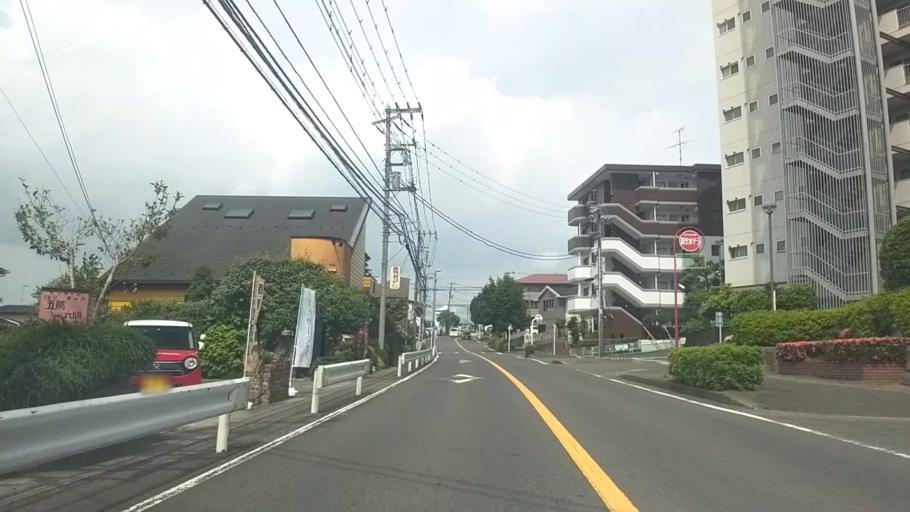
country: JP
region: Kanagawa
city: Fujisawa
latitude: 35.3866
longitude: 139.4708
